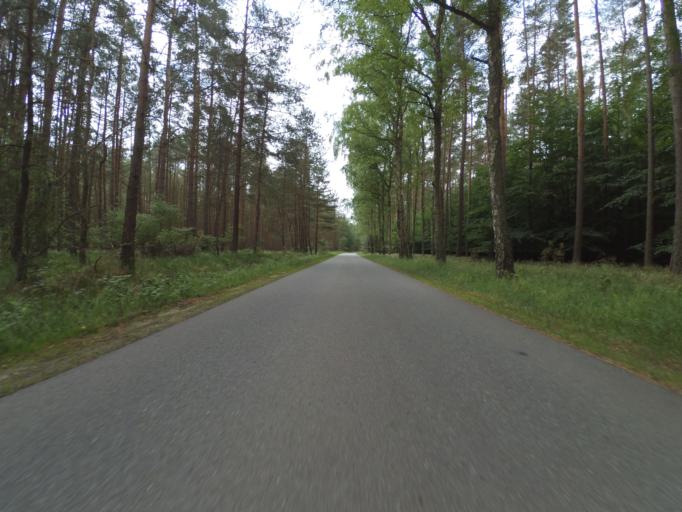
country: DE
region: Mecklenburg-Vorpommern
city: Malchow
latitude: 53.5794
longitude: 12.3728
